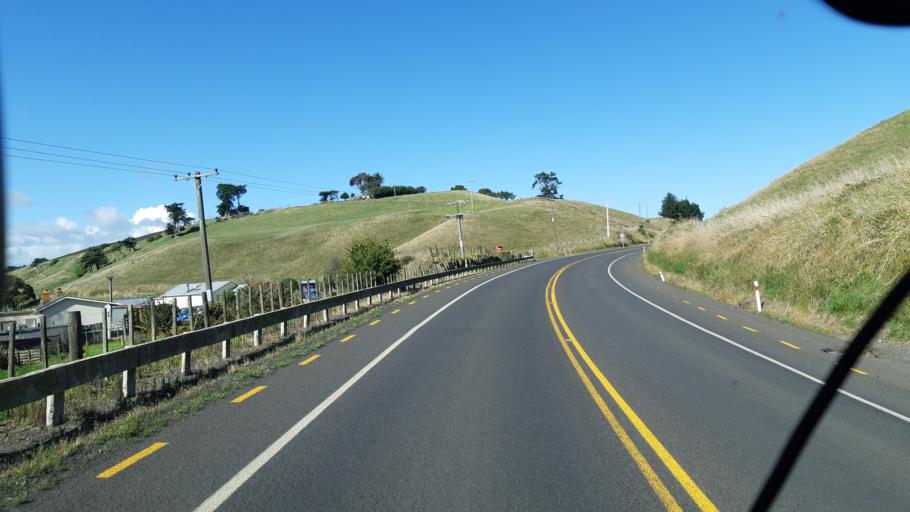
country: NZ
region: Manawatu-Wanganui
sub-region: Wanganui District
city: Wanganui
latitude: -39.9618
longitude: 175.0994
